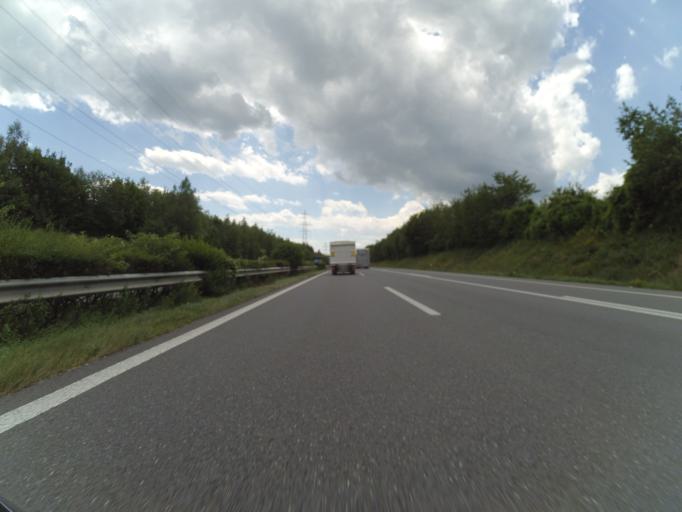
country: CH
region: Vaud
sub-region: Jura-Nord vaudois District
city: Chavornay
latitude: 46.7032
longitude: 6.5775
